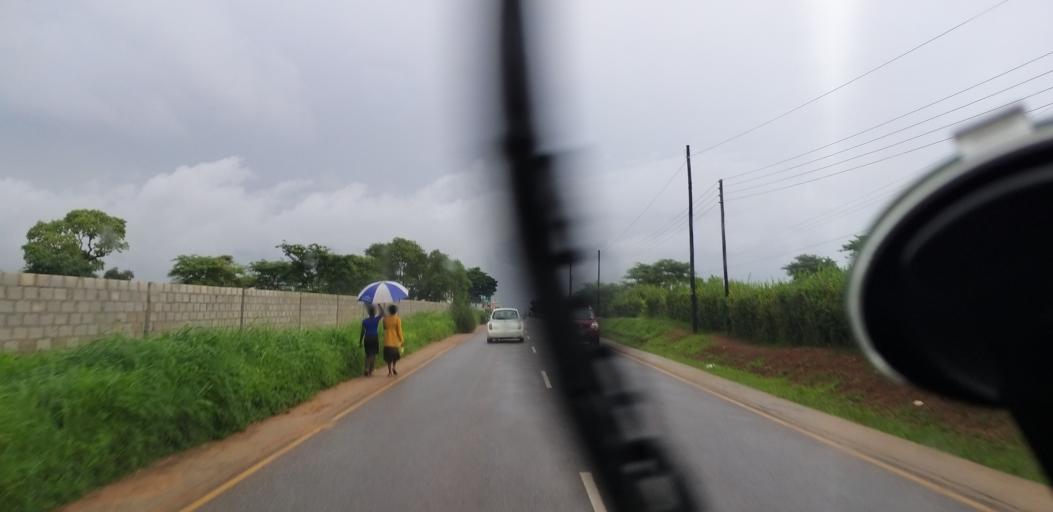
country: ZM
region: Lusaka
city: Lusaka
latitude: -15.5116
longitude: 28.3114
